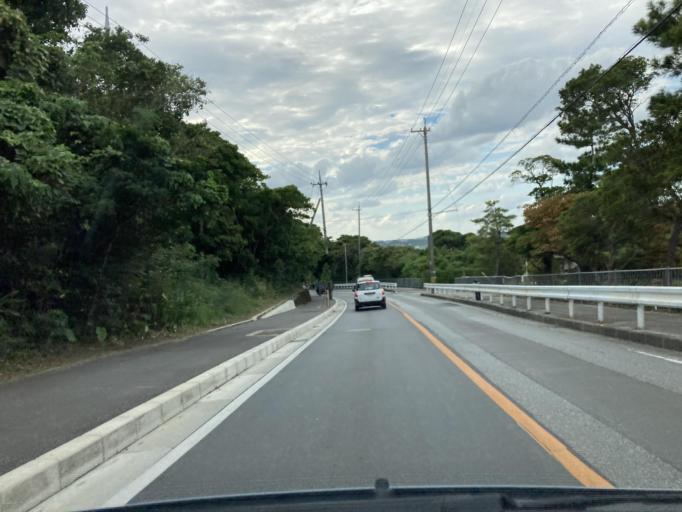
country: JP
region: Okinawa
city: Katsuren-haebaru
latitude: 26.3328
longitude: 127.8787
